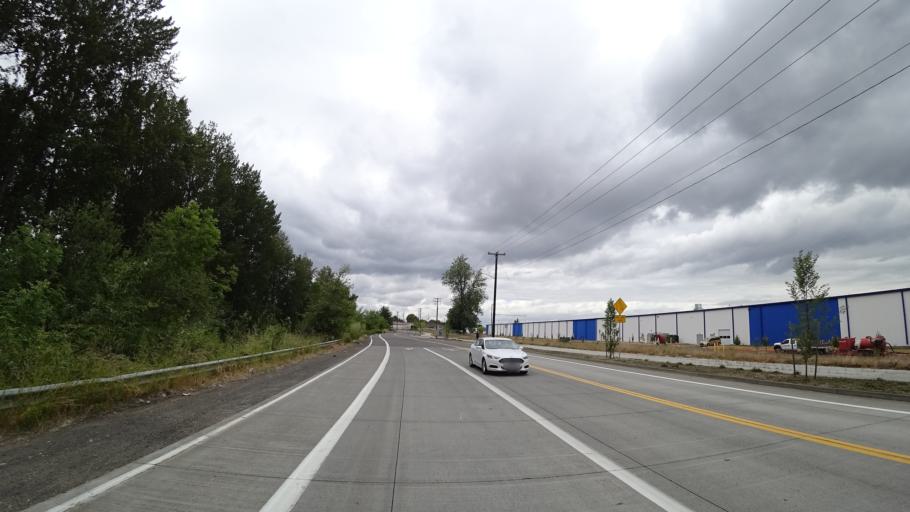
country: US
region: Washington
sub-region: Clark County
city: Walnut Grove
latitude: 45.5734
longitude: -122.5869
